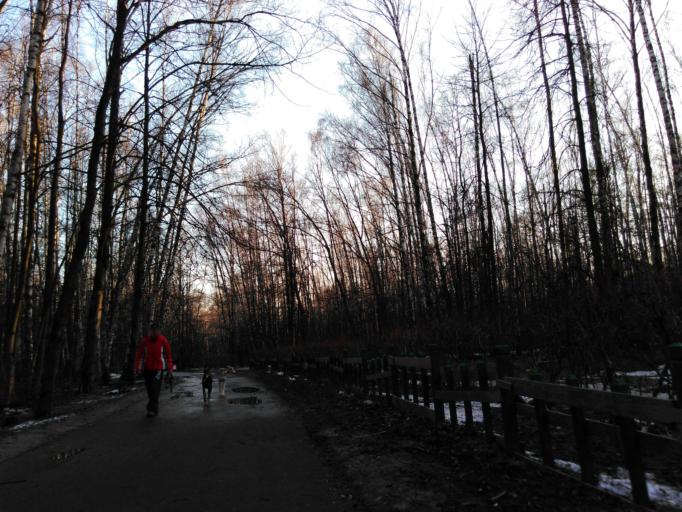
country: RU
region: Moscow
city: Zyuzino
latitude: 55.6452
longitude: 37.5671
